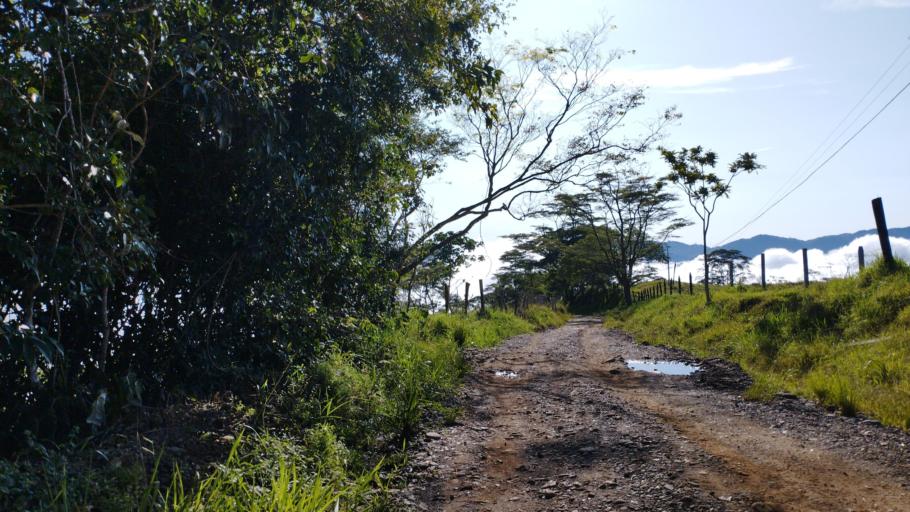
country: CO
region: Casanare
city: Sabanalarga
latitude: 4.7787
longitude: -73.0826
